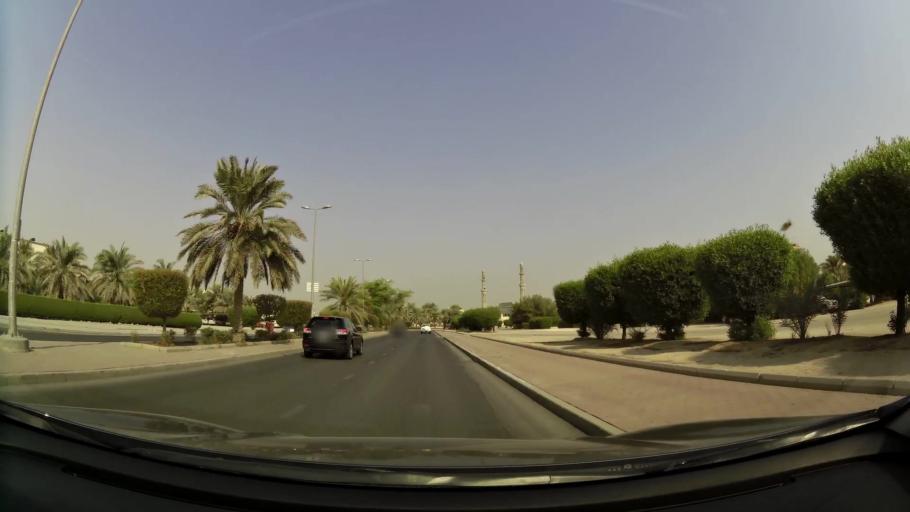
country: KW
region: Al Asimah
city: Ar Rabiyah
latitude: 29.2874
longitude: 47.8723
